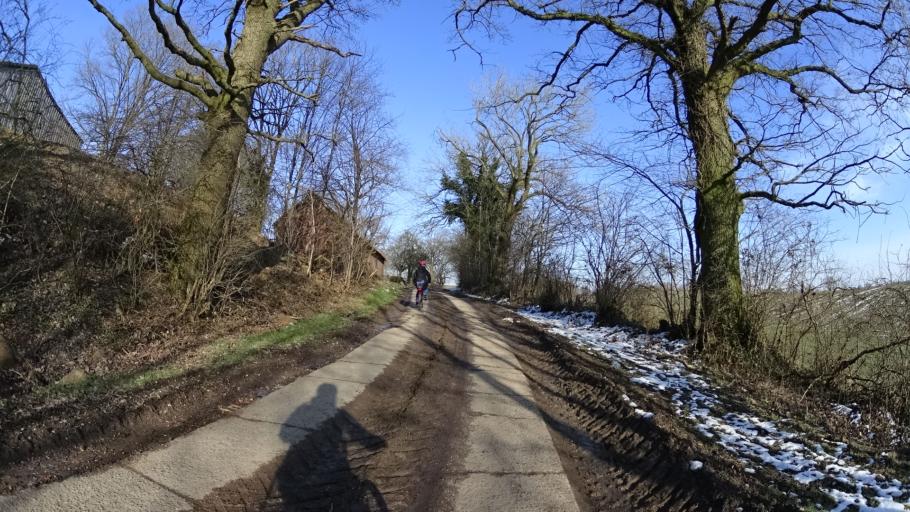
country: DE
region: Schleswig-Holstein
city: Martensrade
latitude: 54.2784
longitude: 10.3819
